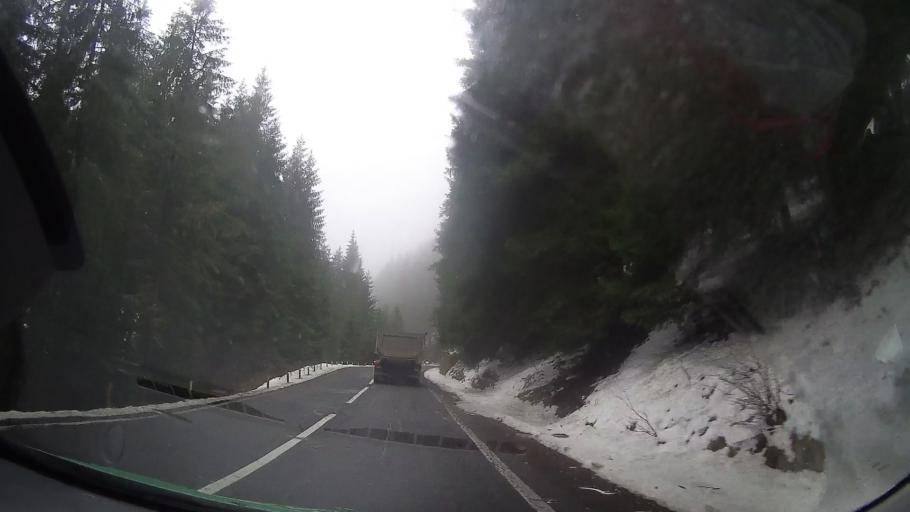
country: RO
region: Harghita
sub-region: Municipiul Gheorgheni
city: Gheorgheni
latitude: 46.7754
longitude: 25.7342
